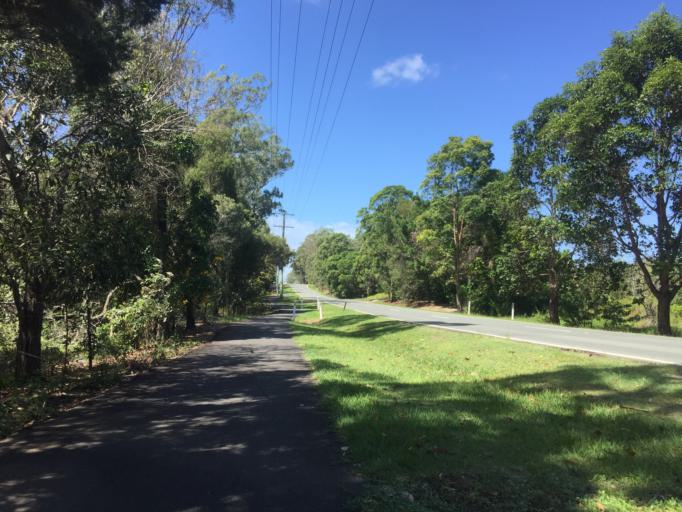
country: AU
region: Queensland
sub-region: Moreton Bay
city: Morayfield
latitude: -27.1107
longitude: 152.9371
